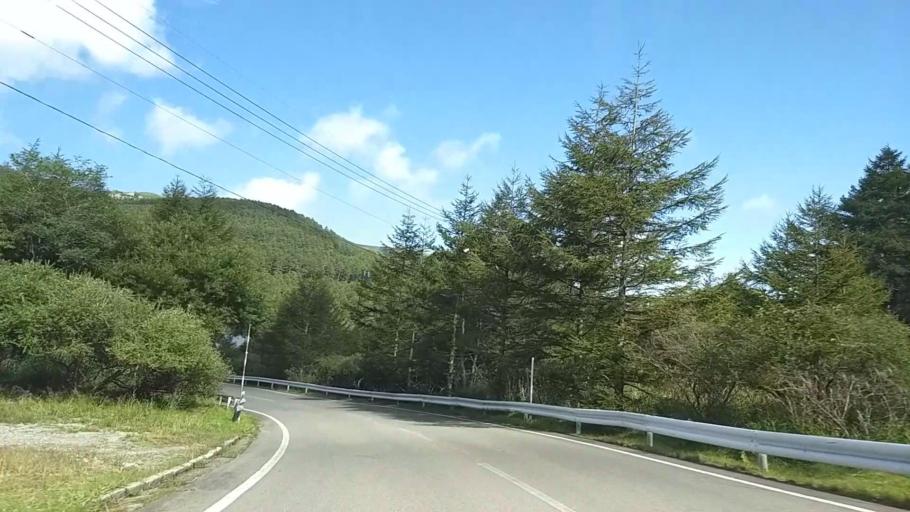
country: JP
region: Nagano
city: Suwa
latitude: 36.1461
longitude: 138.1447
